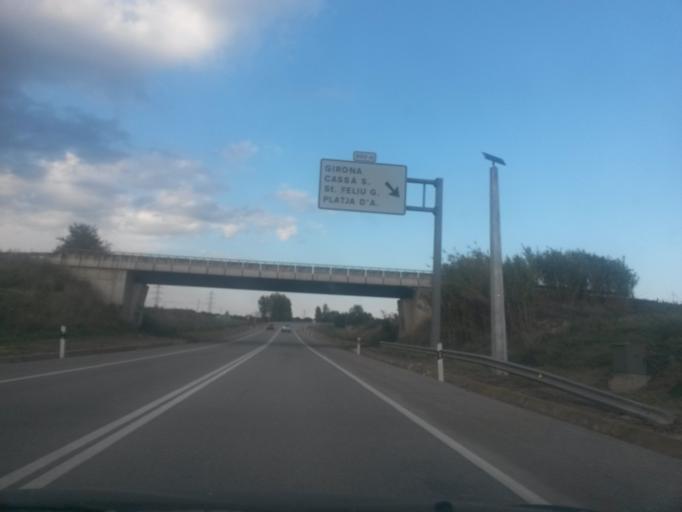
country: ES
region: Catalonia
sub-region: Provincia de Girona
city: Vilobi d'Onyar
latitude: 41.8885
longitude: 2.7728
